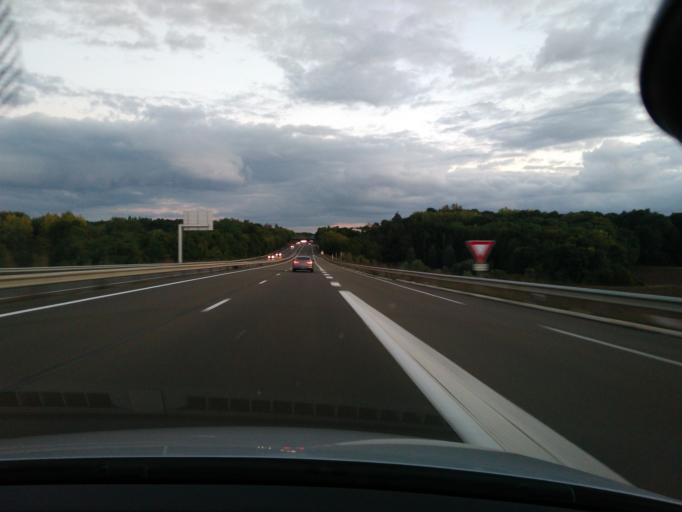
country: FR
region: Ile-de-France
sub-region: Departement de Seine-et-Marne
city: Quincy-Voisins
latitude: 48.9033
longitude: 2.8882
